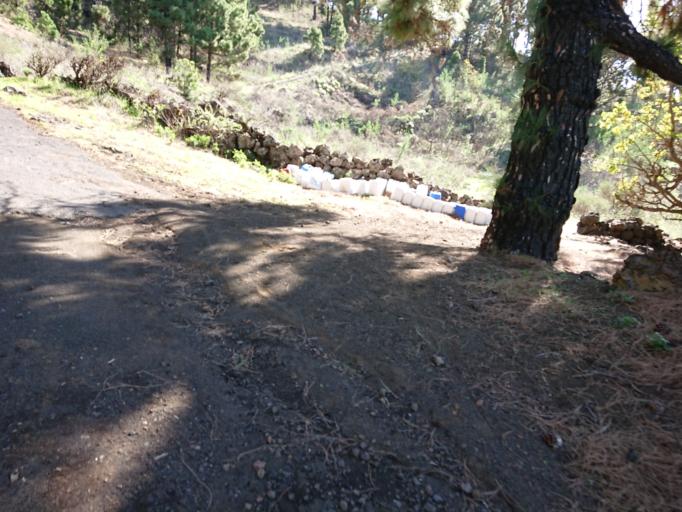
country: ES
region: Canary Islands
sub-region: Provincia de Santa Cruz de Tenerife
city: El Paso
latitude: 28.6061
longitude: -17.8665
